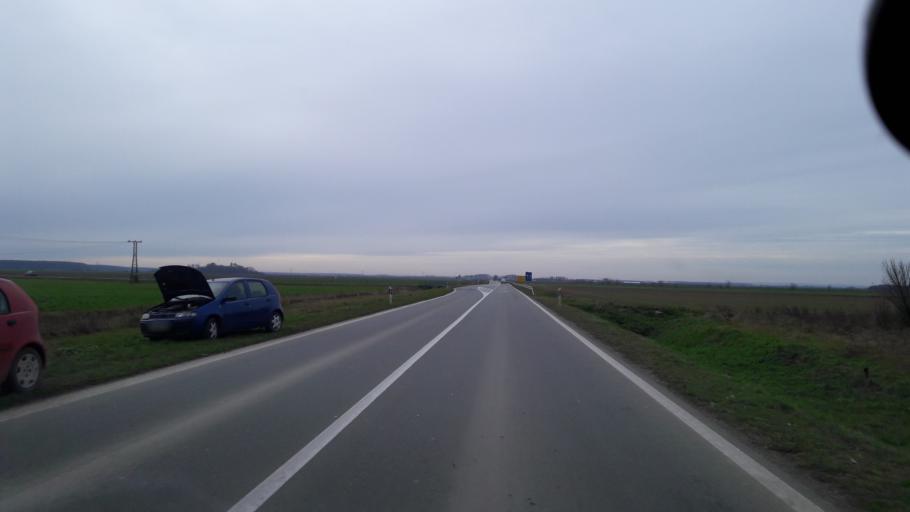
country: HR
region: Osjecko-Baranjska
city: Ovcara
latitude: 45.4906
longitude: 18.5502
